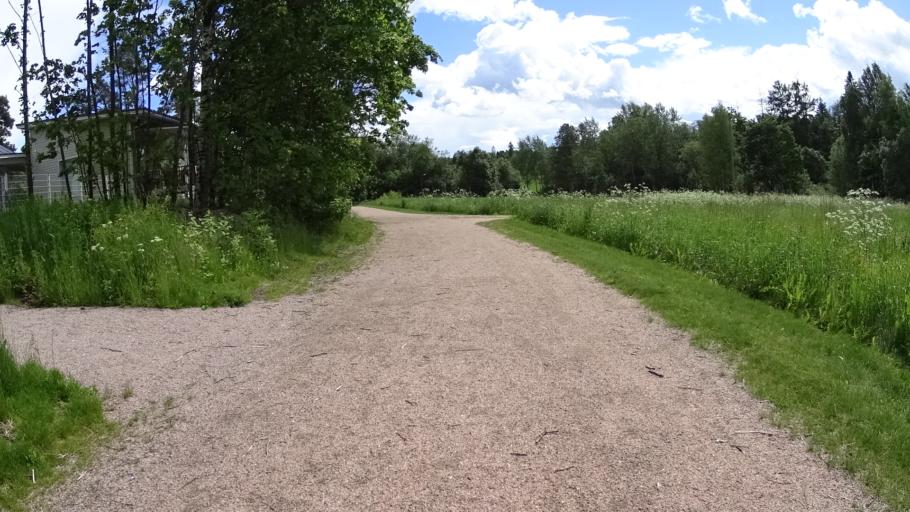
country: FI
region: Uusimaa
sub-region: Helsinki
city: Kauniainen
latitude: 60.2289
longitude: 24.6949
